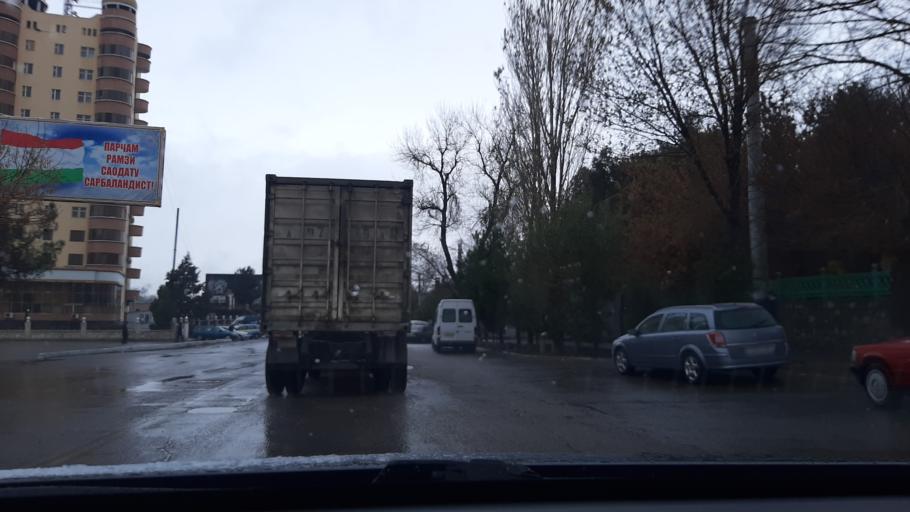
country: TJ
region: Viloyati Sughd
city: Khujand
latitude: 40.2725
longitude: 69.6431
